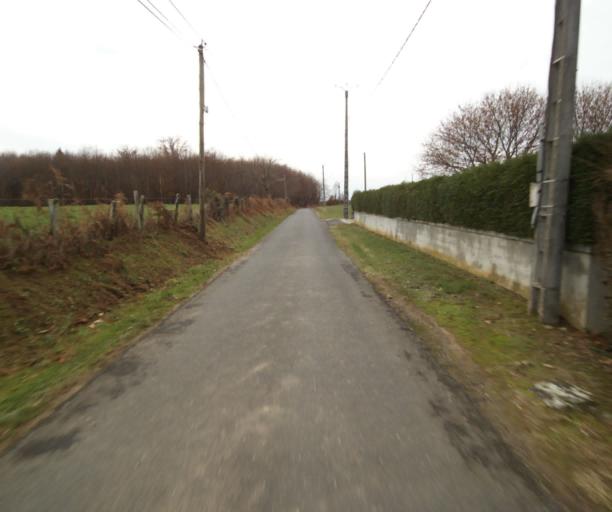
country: FR
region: Limousin
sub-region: Departement de la Correze
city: Chameyrat
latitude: 45.2349
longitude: 1.6839
